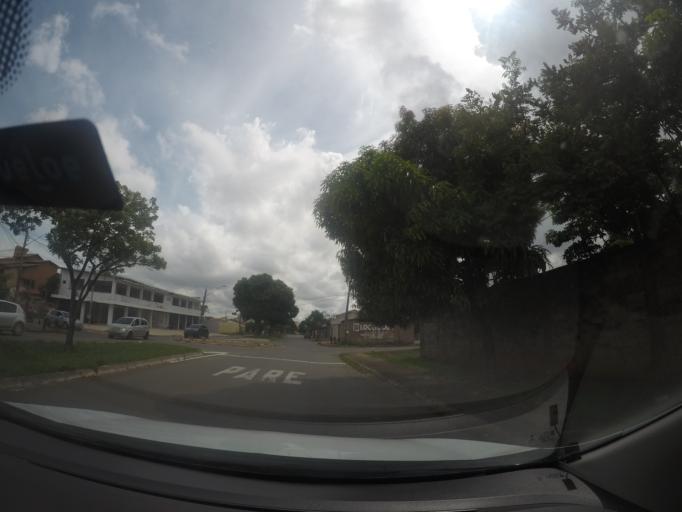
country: BR
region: Goias
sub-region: Goiania
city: Goiania
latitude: -16.7183
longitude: -49.3052
